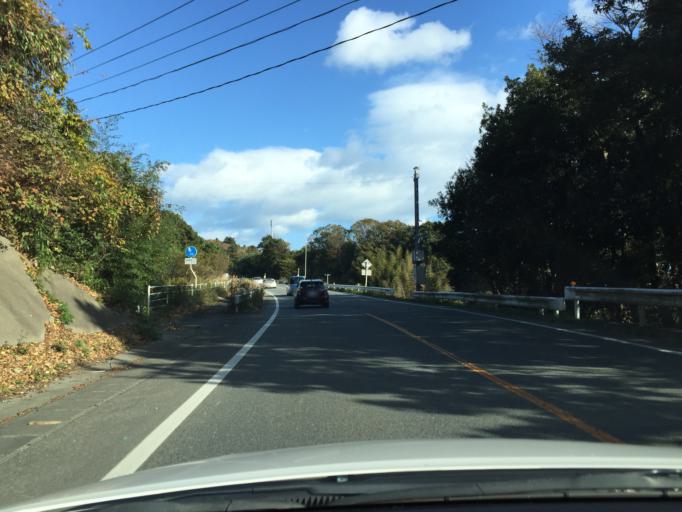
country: JP
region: Fukushima
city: Iwaki
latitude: 37.1907
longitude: 140.9990
